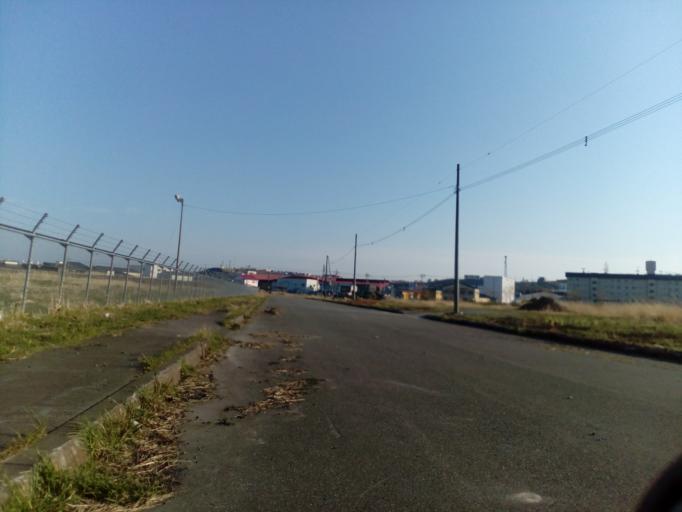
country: JP
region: Hokkaido
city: Wakkanai
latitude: 45.4045
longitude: 141.6877
